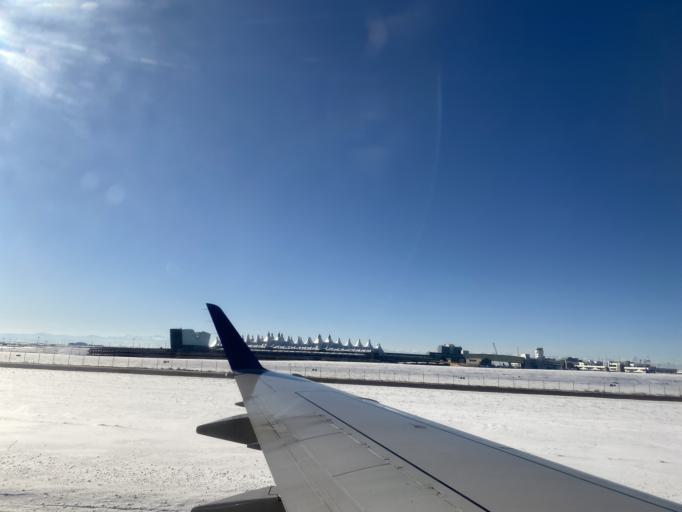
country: US
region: Colorado
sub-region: Weld County
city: Lochbuie
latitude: 39.8498
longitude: -104.6624
